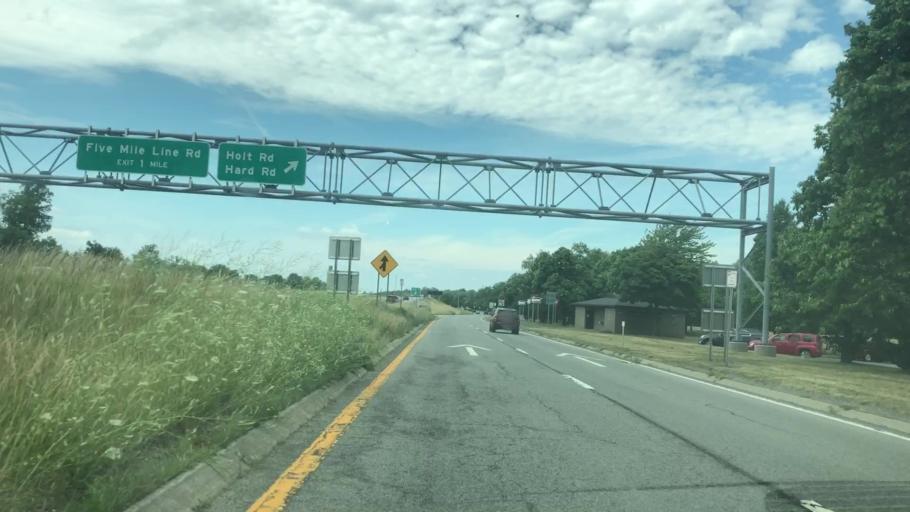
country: US
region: New York
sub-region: Monroe County
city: Webster
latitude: 43.2158
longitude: -77.4399
